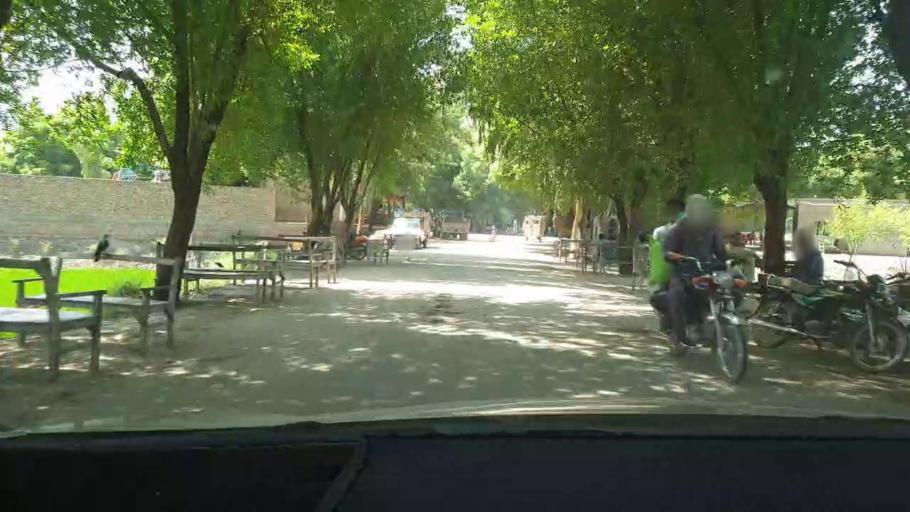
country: PK
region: Sindh
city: Kambar
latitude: 27.6715
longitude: 68.0499
